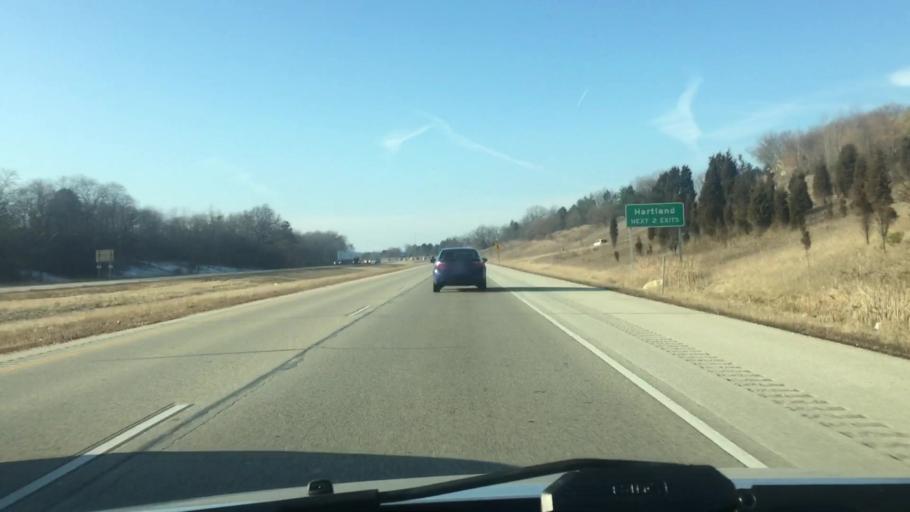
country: US
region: Wisconsin
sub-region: Waukesha County
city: Hartland
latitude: 43.1055
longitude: -88.3142
